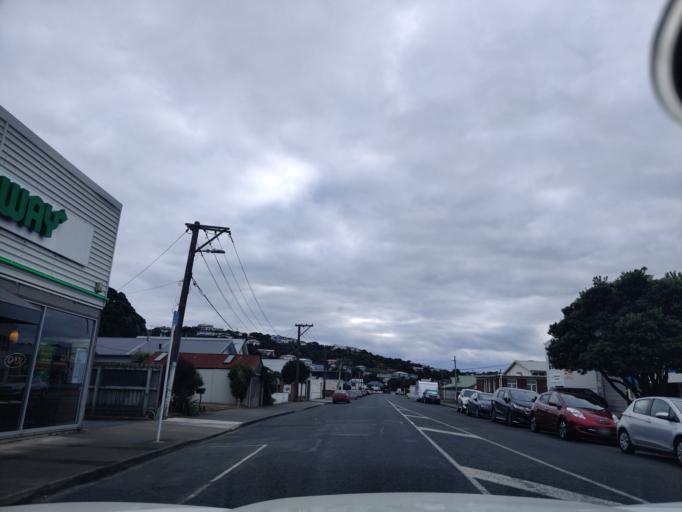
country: NZ
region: Wellington
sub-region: Wellington City
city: Wellington
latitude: -41.3139
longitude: 174.8143
